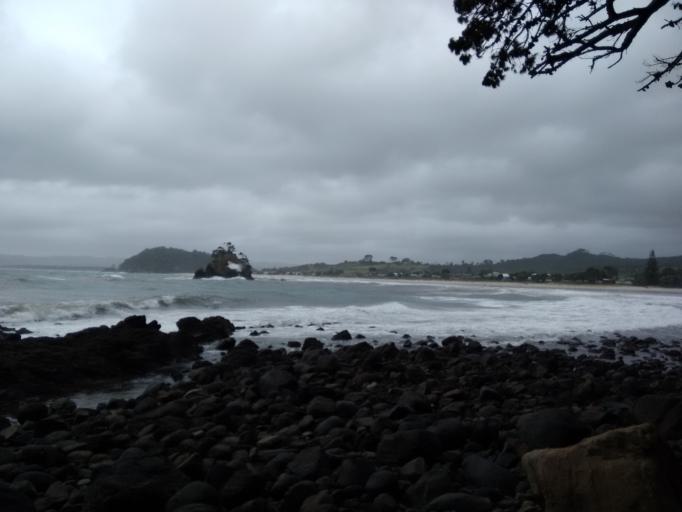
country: NZ
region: Waikato
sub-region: Thames-Coromandel District
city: Coromandel
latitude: -36.7044
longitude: 175.6101
